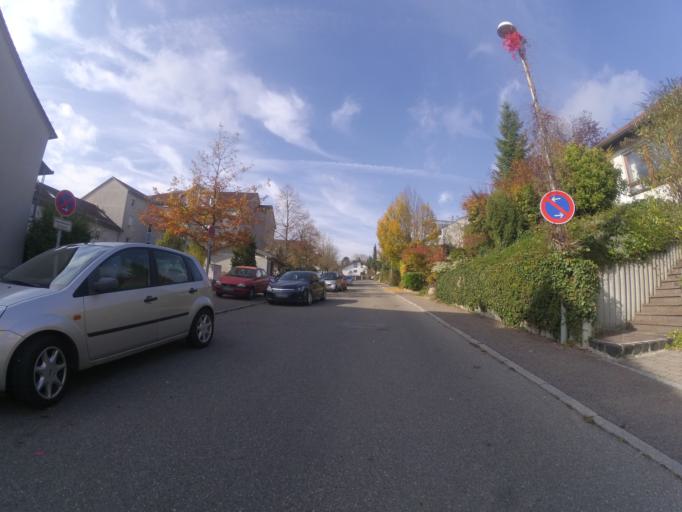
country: DE
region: Baden-Wuerttemberg
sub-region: Tuebingen Region
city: Ulm
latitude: 48.4147
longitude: 9.9568
